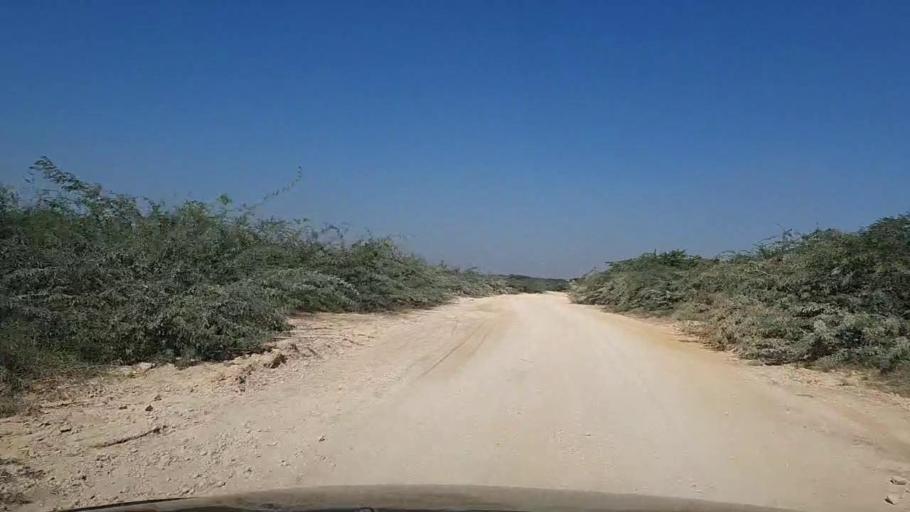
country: PK
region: Sindh
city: Thatta
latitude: 24.6222
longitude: 67.8392
